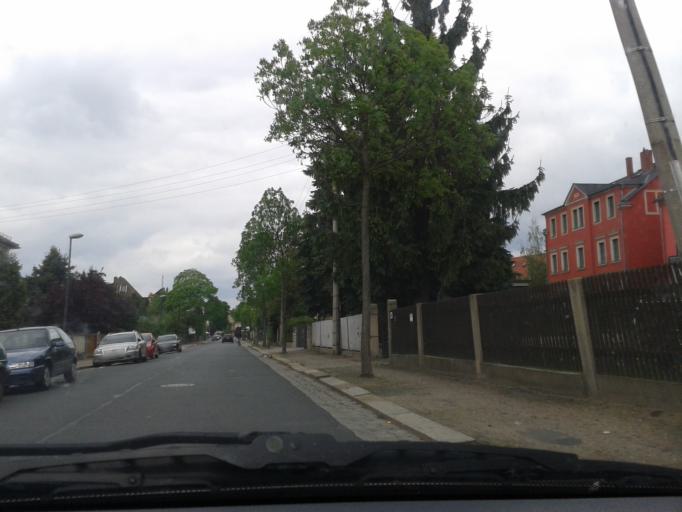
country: DE
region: Saxony
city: Radebeul
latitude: 51.0944
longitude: 13.6818
